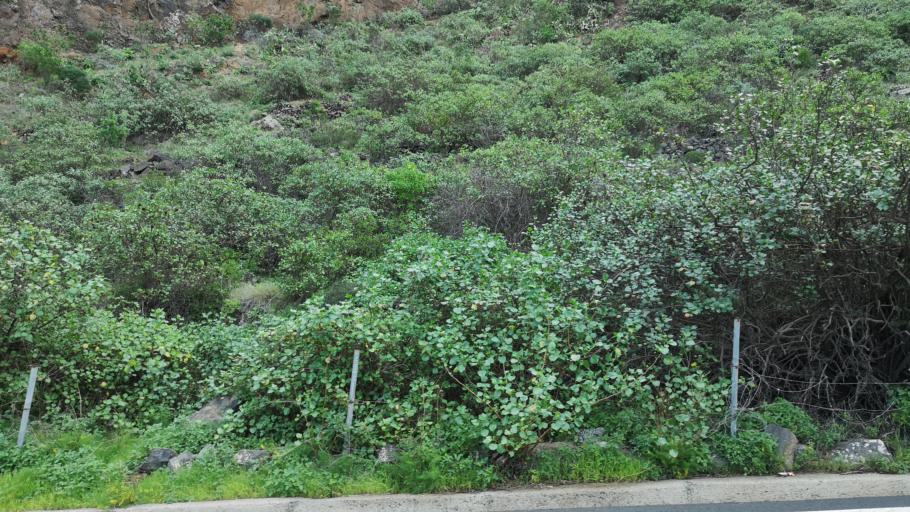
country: ES
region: Canary Islands
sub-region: Provincia de Santa Cruz de Tenerife
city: Agulo
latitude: 28.1919
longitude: -17.1987
